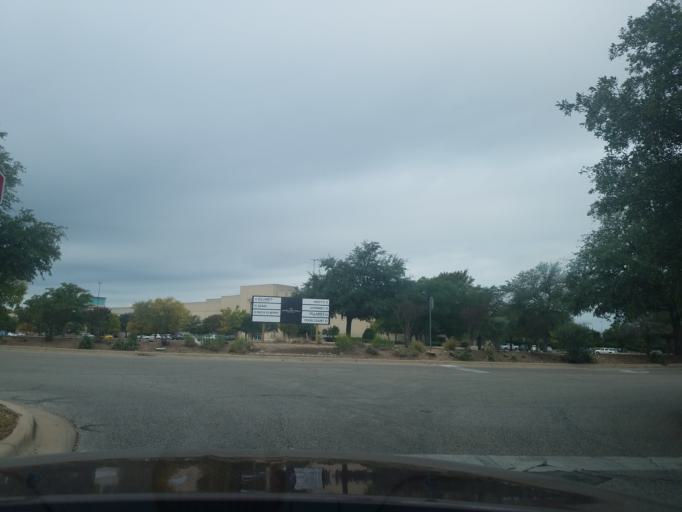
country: US
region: Texas
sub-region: Williamson County
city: Anderson Mill
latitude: 30.4714
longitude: -97.8036
